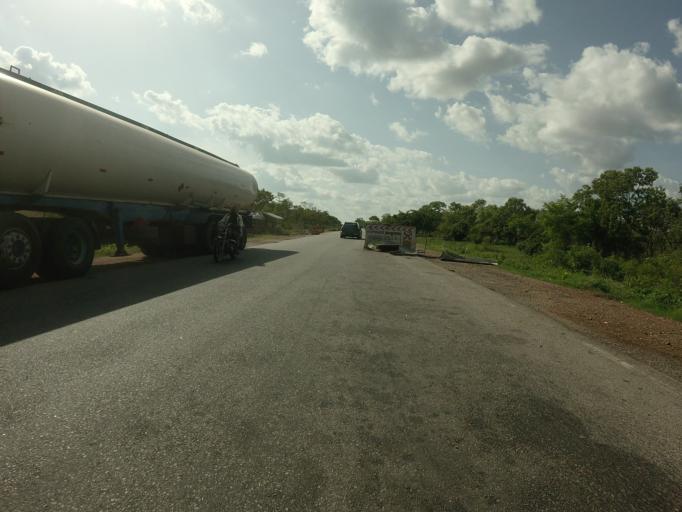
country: GH
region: Upper East
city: Bolgatanga
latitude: 10.5238
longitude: -0.8144
